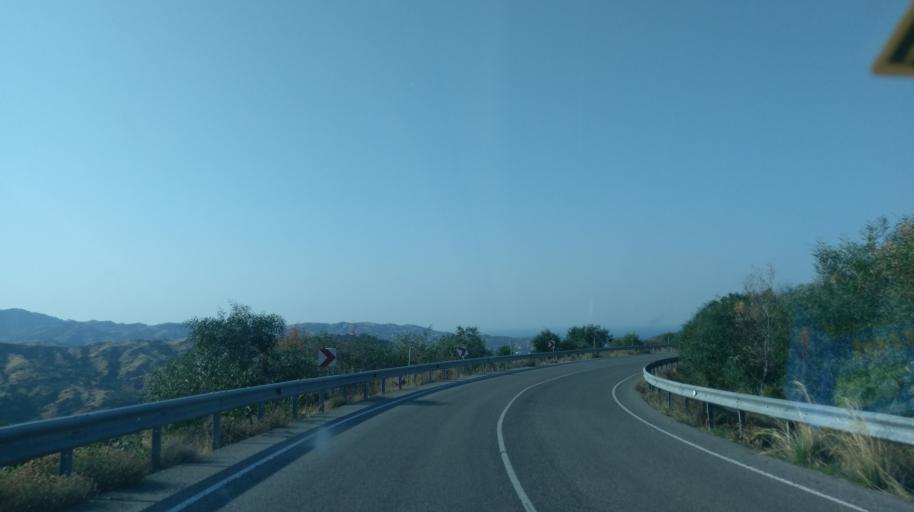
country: CY
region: Lefkosia
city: Kato Pyrgos
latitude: 35.1665
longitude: 32.7095
